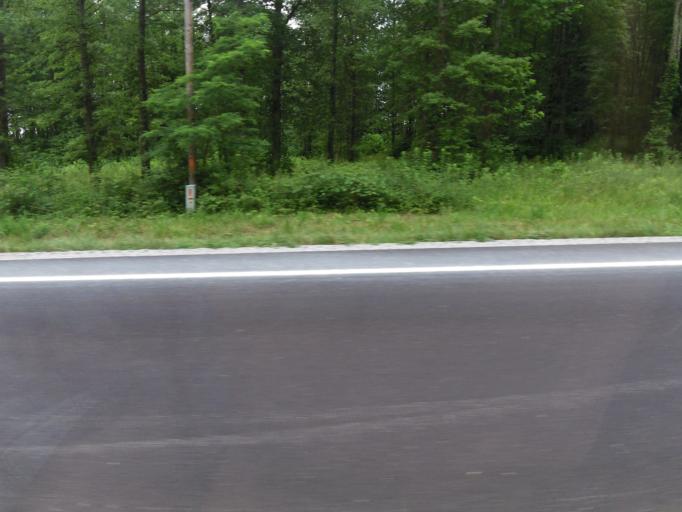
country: US
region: Ohio
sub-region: Clinton County
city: Blanchester
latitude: 39.2159
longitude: -83.9128
